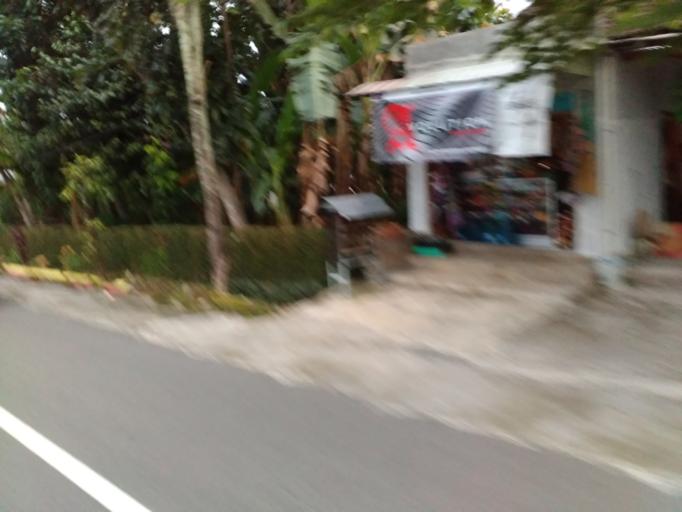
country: ID
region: Central Java
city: Boyolali
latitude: -7.5361
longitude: 110.6075
